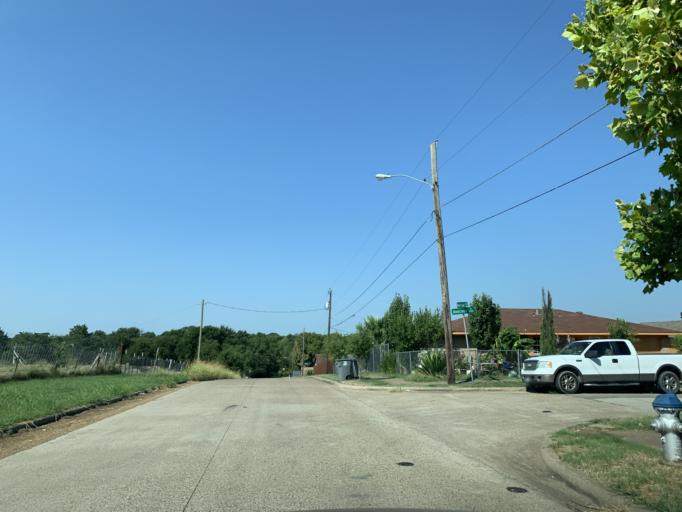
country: US
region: Texas
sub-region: Dallas County
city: Hutchins
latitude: 32.6654
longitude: -96.7473
